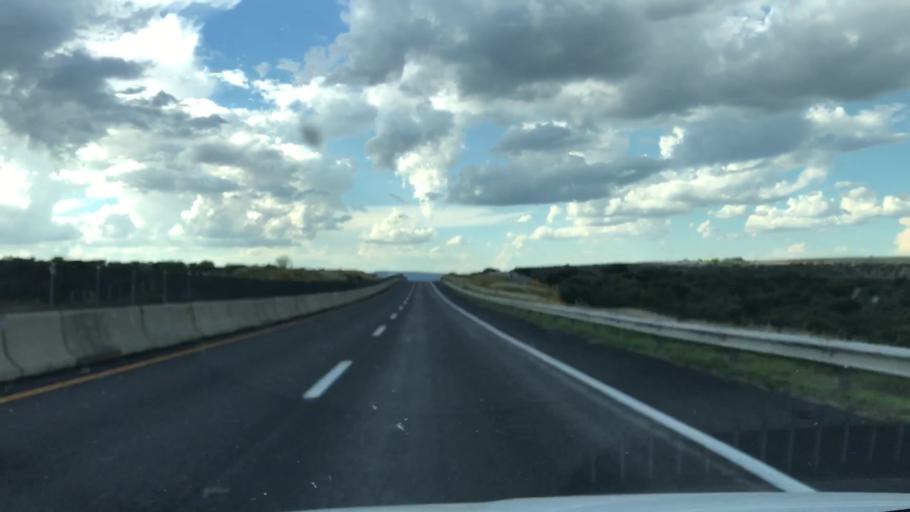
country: MX
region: Guanajuato
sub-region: Leon
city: Rizos de la Joya (Rizos del Saucillo)
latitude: 21.1321
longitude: -101.8226
